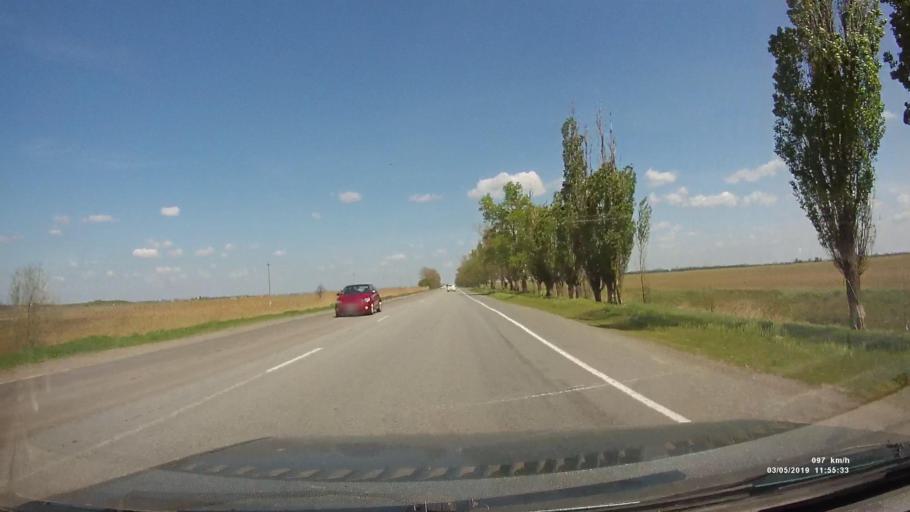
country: RU
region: Rostov
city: Bagayevskaya
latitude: 47.1826
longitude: 40.2923
